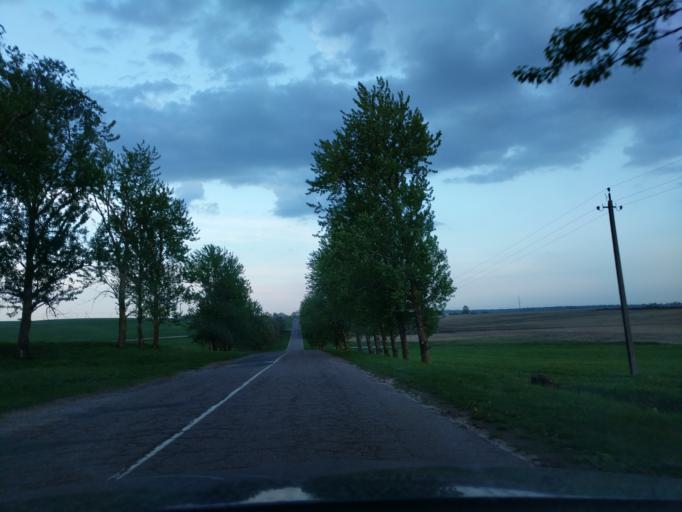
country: BY
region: Minsk
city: Novy Svyerzhan'
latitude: 53.4763
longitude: 26.6315
